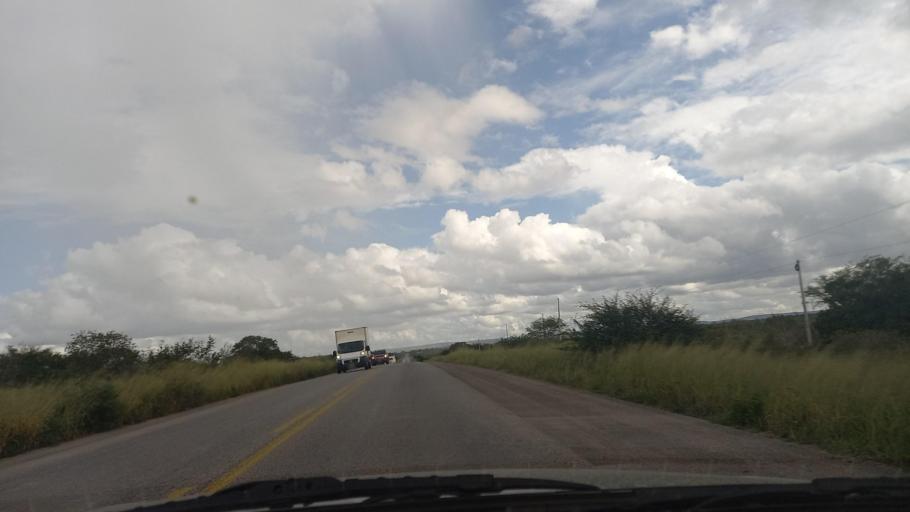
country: BR
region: Pernambuco
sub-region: Cachoeirinha
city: Cachoeirinha
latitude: -8.5452
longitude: -36.2704
